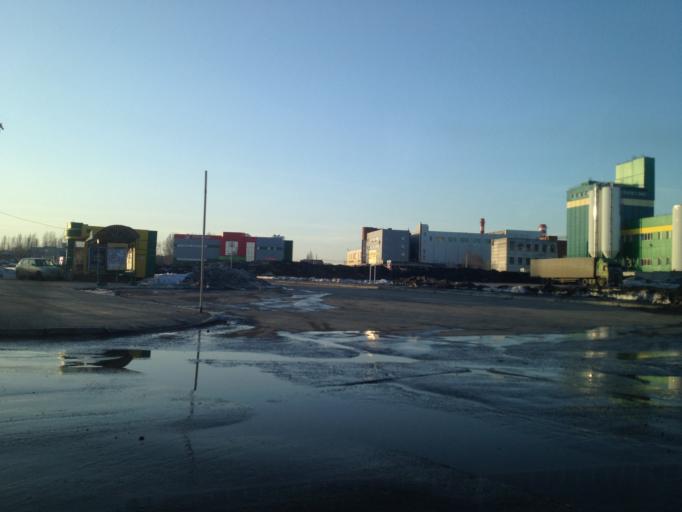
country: RU
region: Sverdlovsk
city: Sovkhoznyy
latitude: 56.7650
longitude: 60.5572
